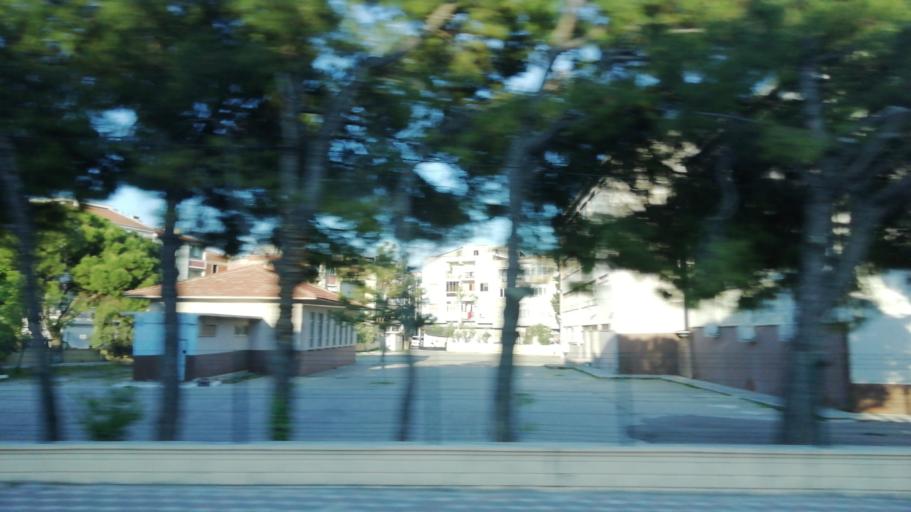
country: TR
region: Manisa
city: Akhisar
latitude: 38.9267
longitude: 27.8346
